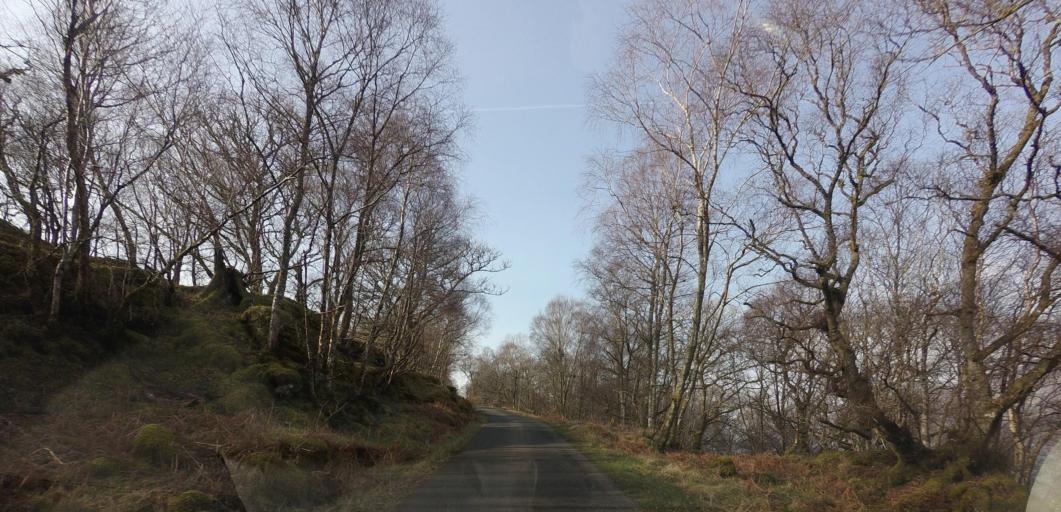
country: GB
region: Scotland
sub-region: Stirling
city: Callander
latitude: 56.4847
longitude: -4.2374
